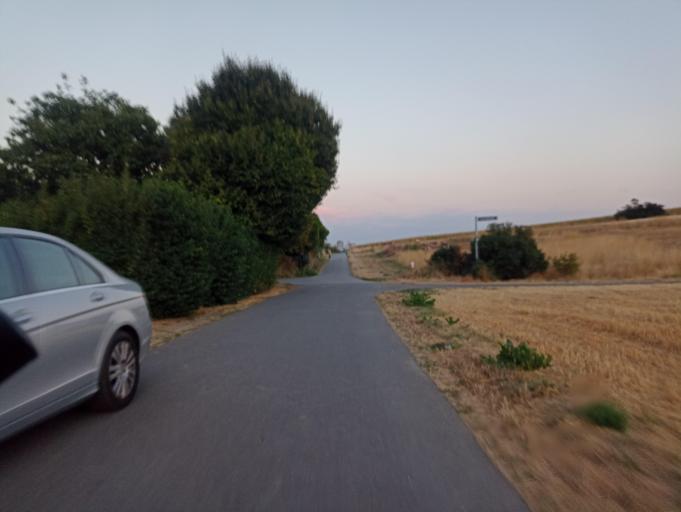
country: DE
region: Hesse
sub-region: Regierungsbezirk Darmstadt
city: Bad Homburg vor der Hoehe
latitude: 50.1849
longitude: 8.6433
